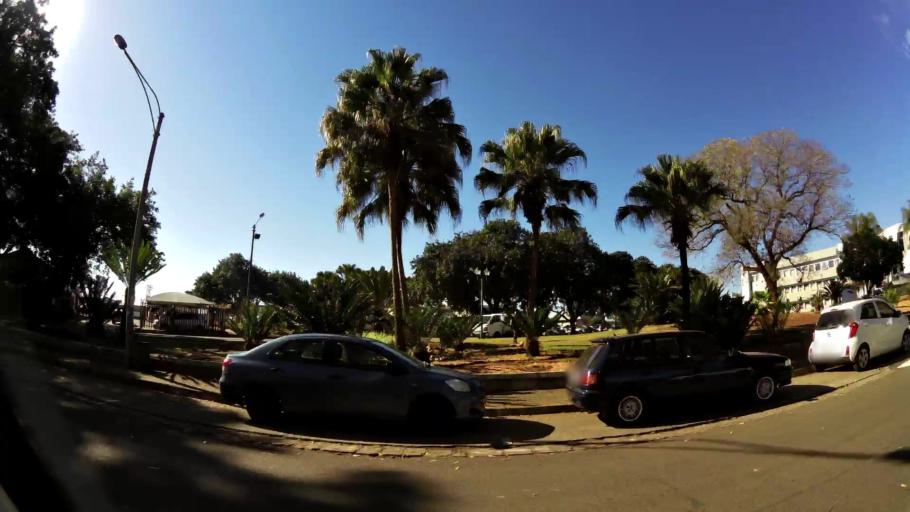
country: ZA
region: Limpopo
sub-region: Mopani District Municipality
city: Tzaneen
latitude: -23.8287
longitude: 30.1584
